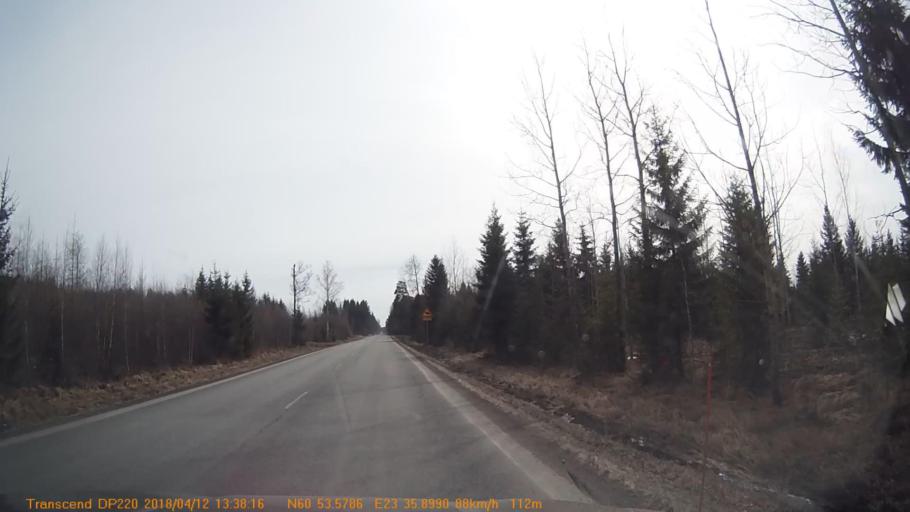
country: FI
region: Haeme
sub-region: Forssa
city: Forssa
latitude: 60.8927
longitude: 23.5984
